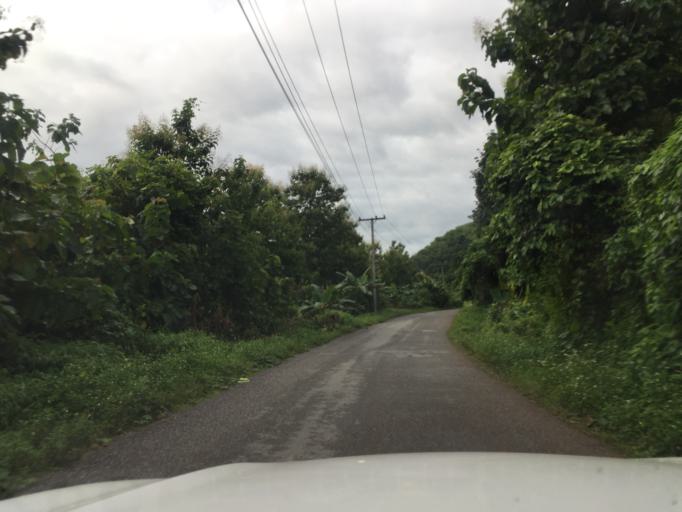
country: LA
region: Oudomxai
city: Muang La
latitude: 21.0831
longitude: 102.2424
